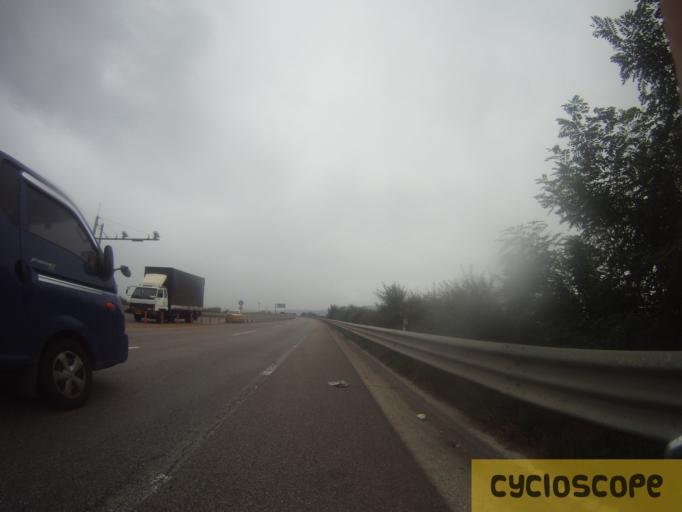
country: KR
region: Gyeonggi-do
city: Hwaseong-si
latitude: 37.1316
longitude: 126.8636
